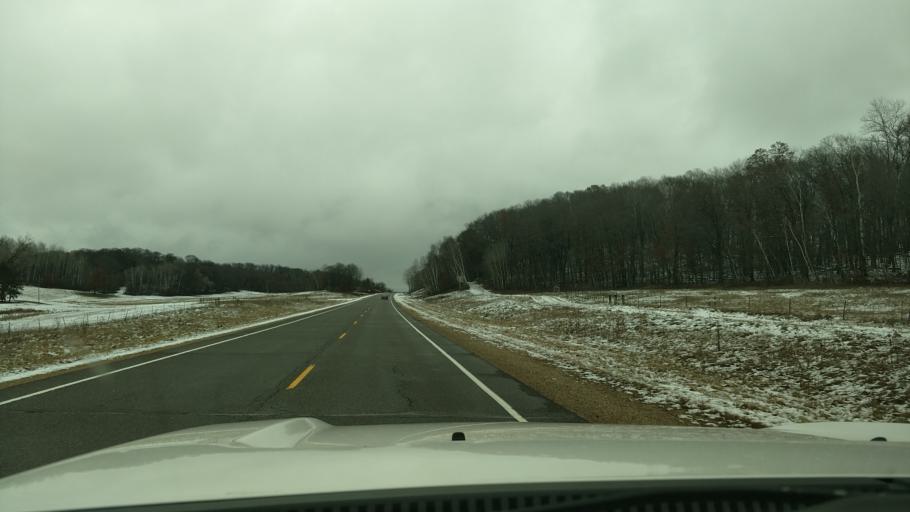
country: US
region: Wisconsin
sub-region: Dunn County
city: Tainter Lake
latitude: 45.1228
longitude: -91.8775
